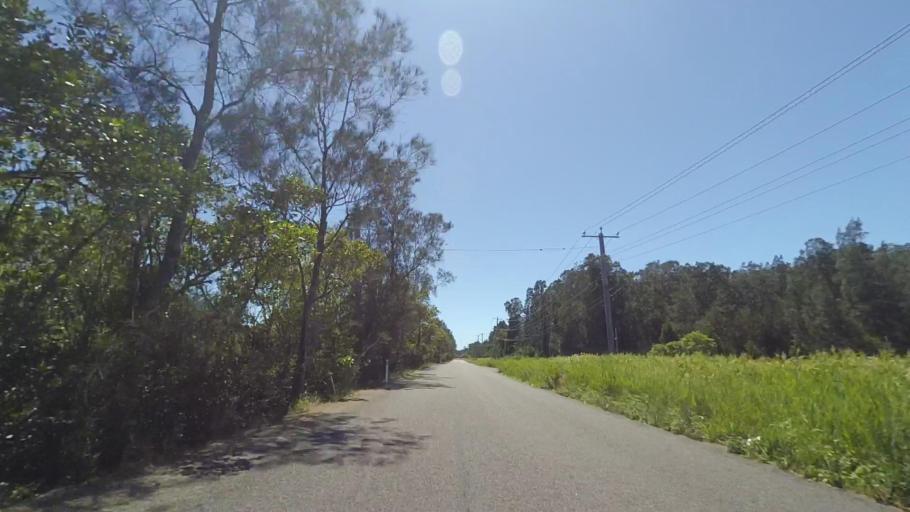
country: AU
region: New South Wales
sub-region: Port Stephens Shire
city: Medowie
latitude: -32.7798
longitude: 151.9589
